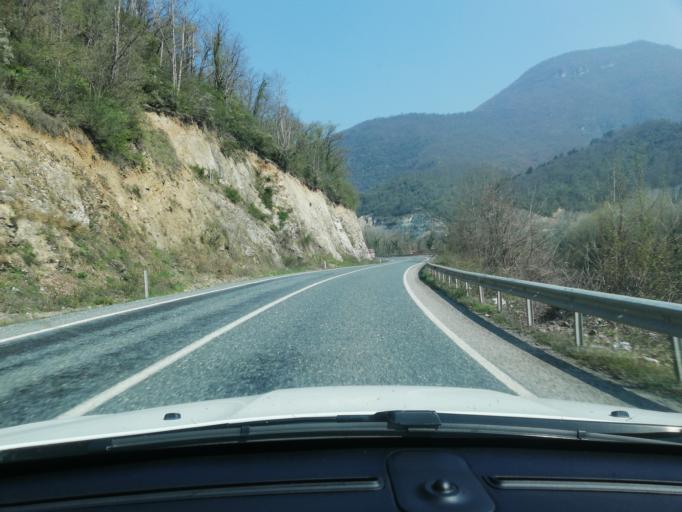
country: TR
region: Zonguldak
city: Gokcebey
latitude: 41.2501
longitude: 32.1654
